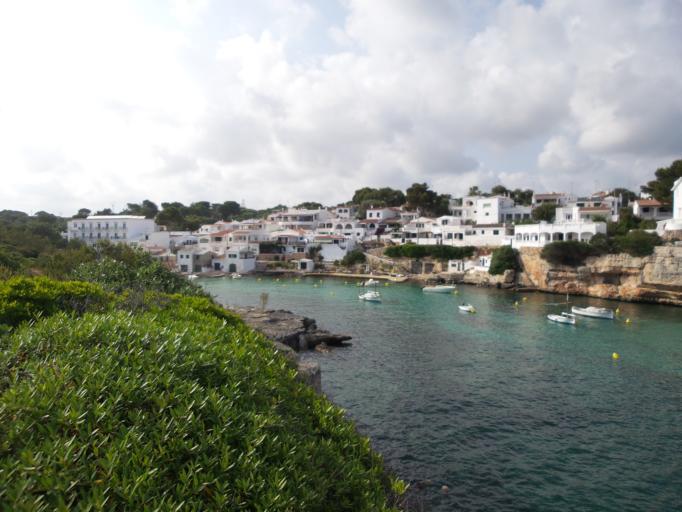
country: ES
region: Balearic Islands
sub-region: Illes Balears
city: Sant Lluis
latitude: 39.8281
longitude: 4.2942
